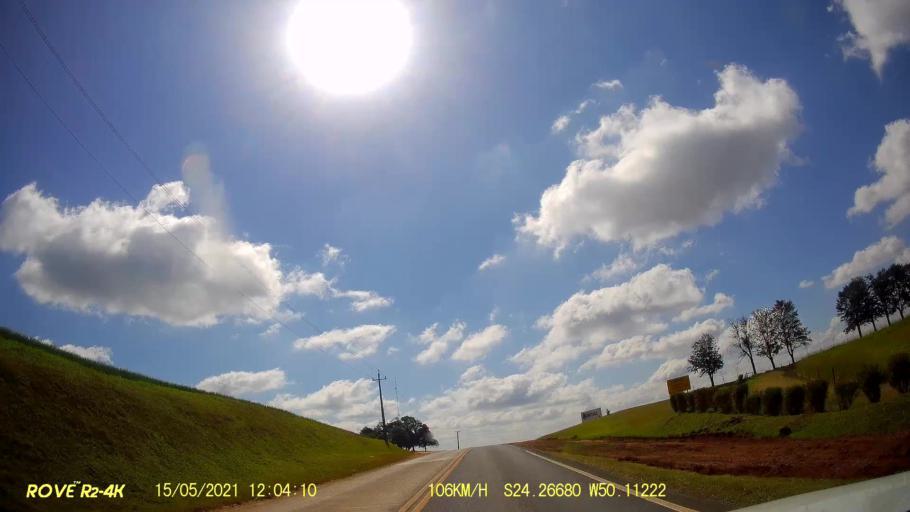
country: BR
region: Parana
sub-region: Pirai Do Sul
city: Pirai do Sul
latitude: -24.2668
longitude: -50.1123
